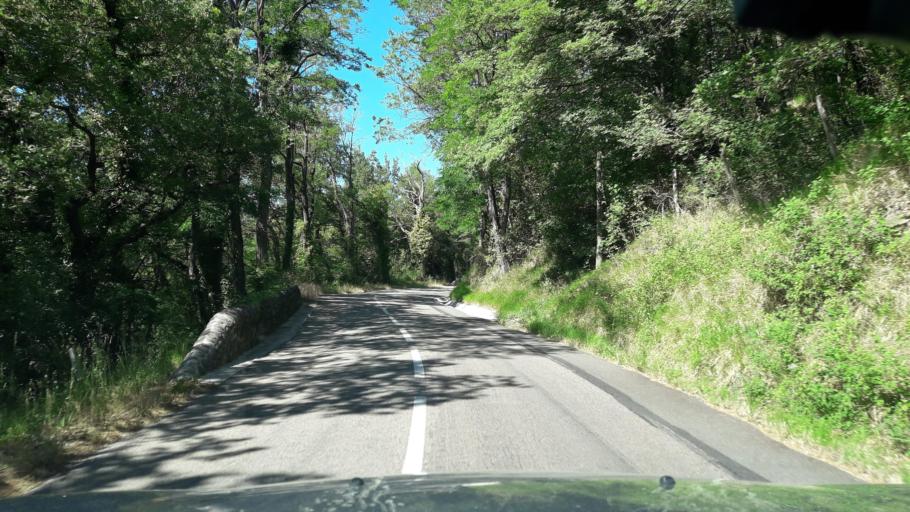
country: FR
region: Rhone-Alpes
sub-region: Departement de l'Ardeche
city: Villeneuve-de-Berg
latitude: 44.6105
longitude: 4.5381
